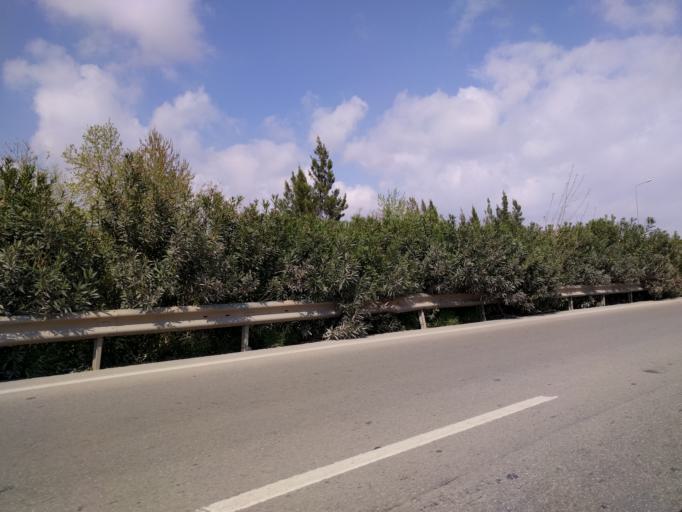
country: TR
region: Antalya
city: Antalya
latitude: 36.9011
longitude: 30.6442
